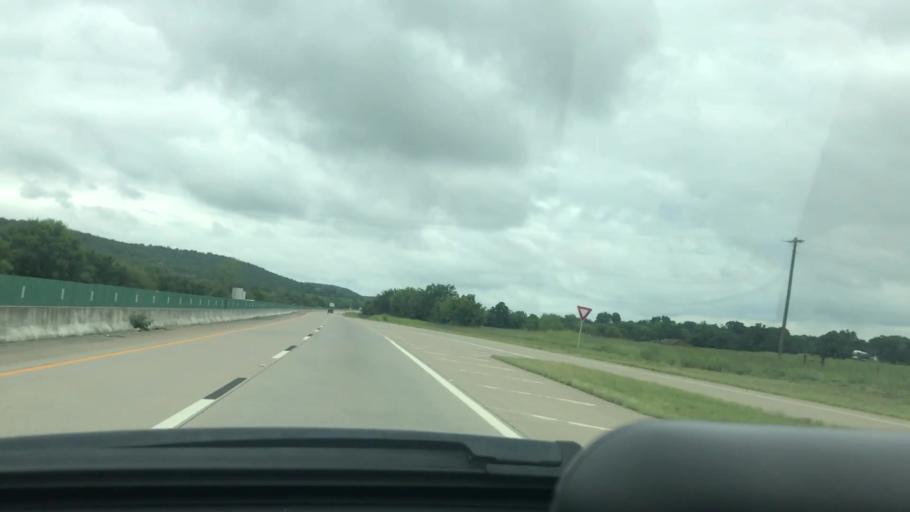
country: US
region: Oklahoma
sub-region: Pittsburg County
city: Krebs
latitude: 35.0611
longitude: -95.7061
